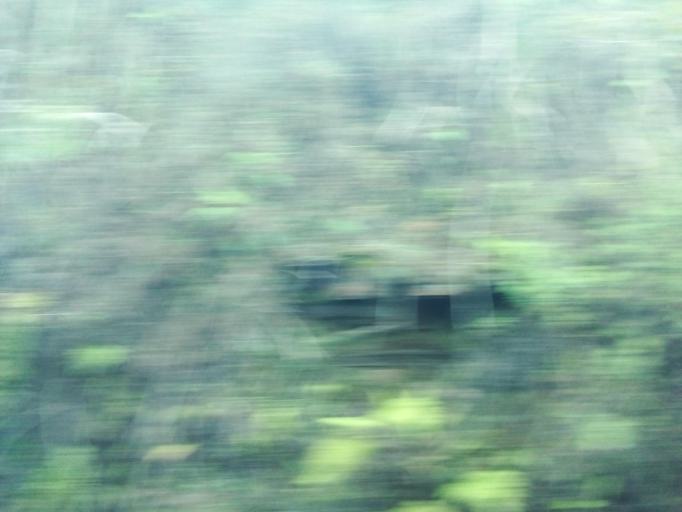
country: BR
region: Minas Gerais
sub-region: Rio Piracicaba
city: Rio Piracicaba
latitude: -19.8913
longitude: -43.1400
